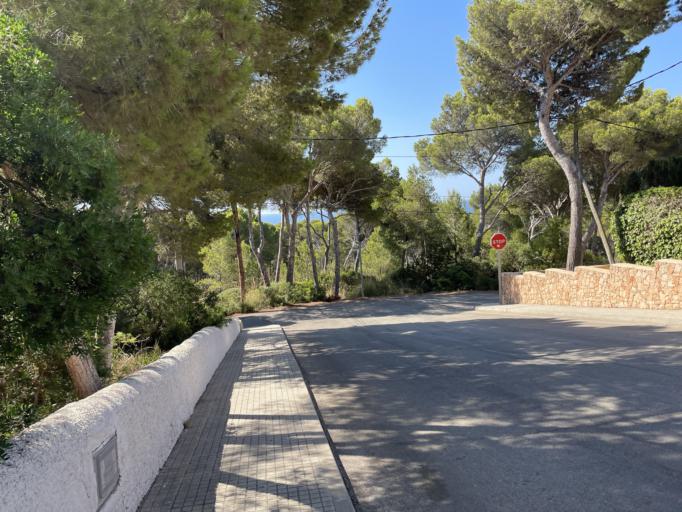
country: ES
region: Balearic Islands
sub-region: Illes Balears
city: Capdepera
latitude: 39.7187
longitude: 3.4689
